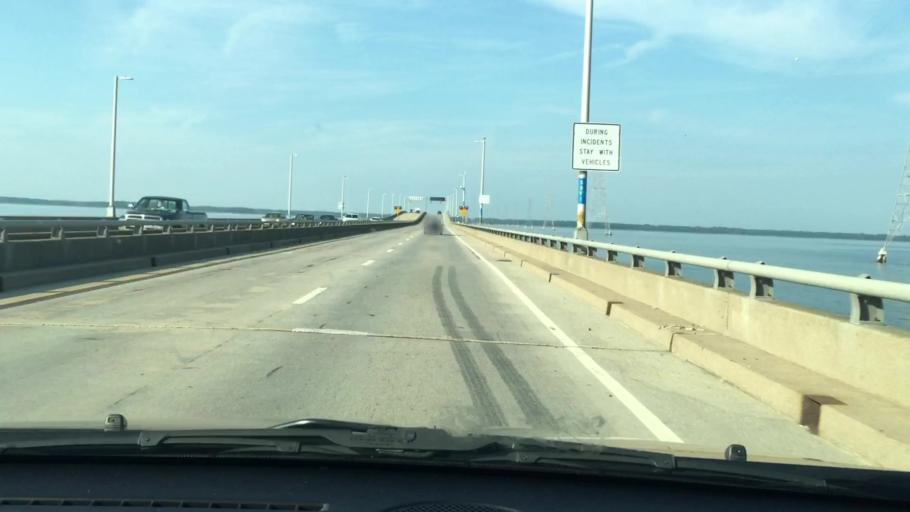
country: US
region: Virginia
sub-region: City of Newport News
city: Newport News
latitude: 36.9987
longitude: -76.4740
